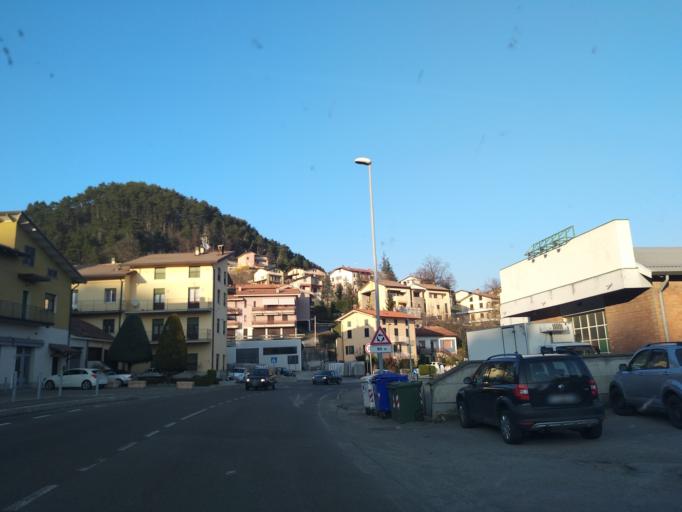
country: IT
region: Emilia-Romagna
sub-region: Provincia di Reggio Emilia
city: Castelnovo ne'Monti
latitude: 44.4310
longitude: 10.3950
